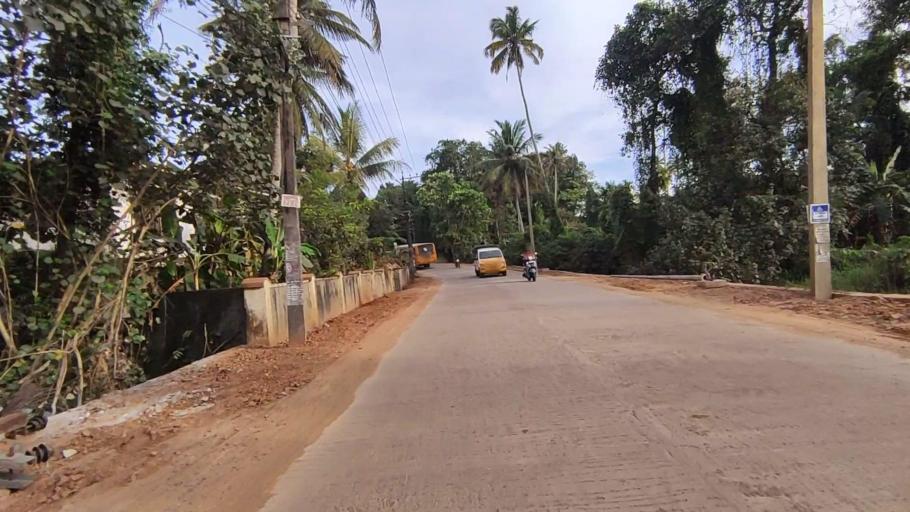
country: IN
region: Kerala
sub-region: Kottayam
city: Kottayam
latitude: 9.6092
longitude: 76.4884
